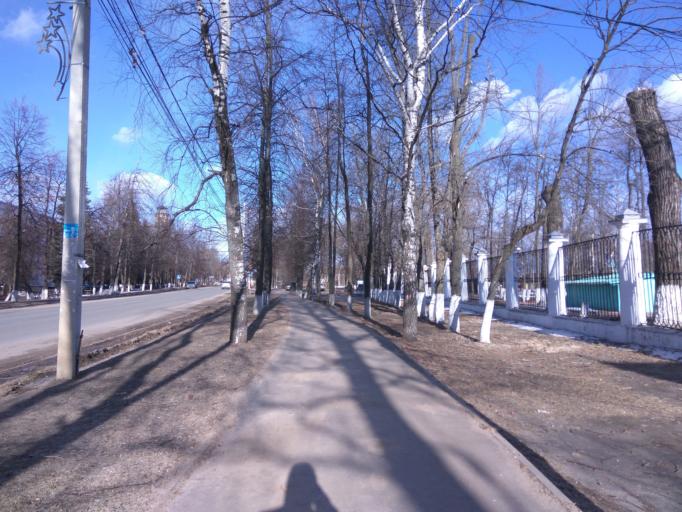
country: RU
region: Jaroslavl
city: Rostov
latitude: 57.1861
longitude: 39.4231
